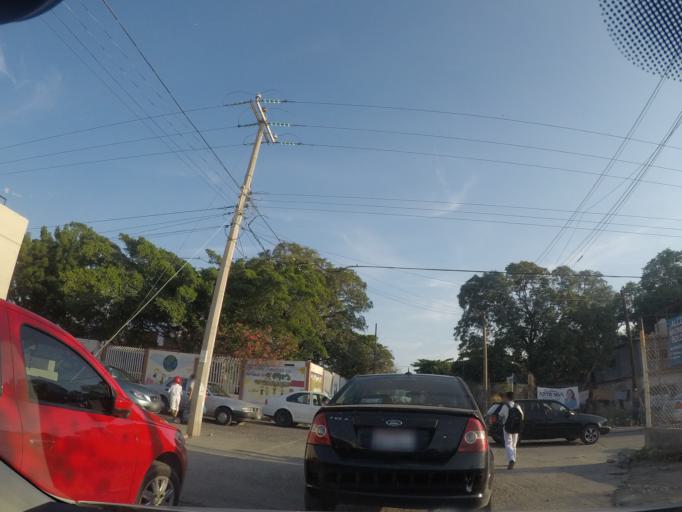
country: MX
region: Oaxaca
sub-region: Salina Cruz
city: Salina Cruz
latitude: 16.2028
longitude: -95.2012
